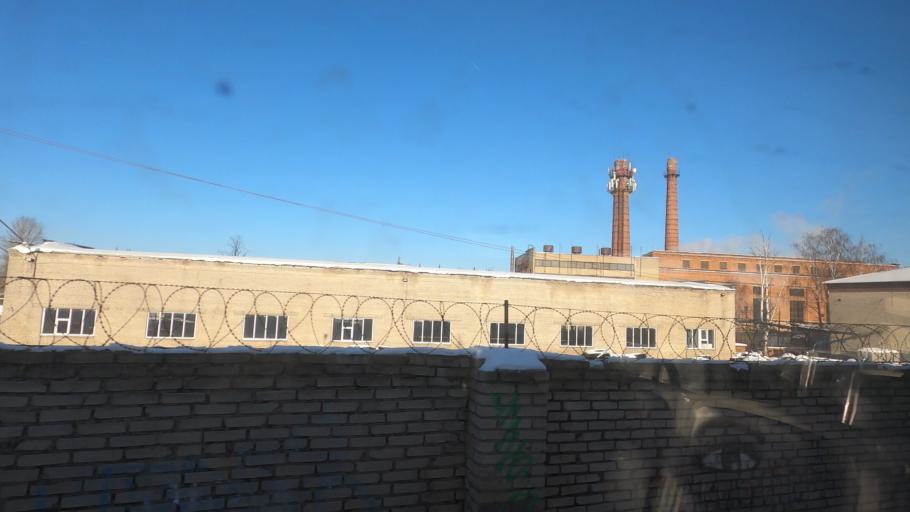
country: RU
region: Moskovskaya
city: Pavlovskiy Posad
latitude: 55.7748
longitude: 38.6885
